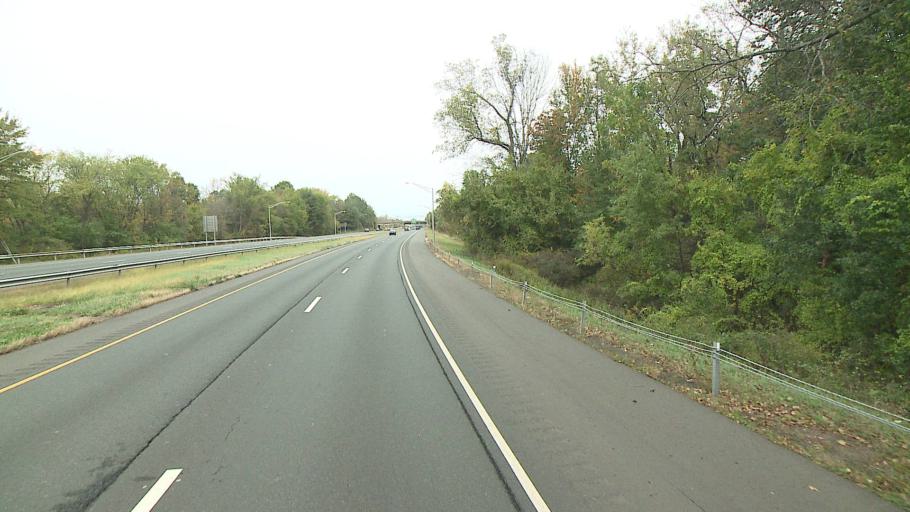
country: US
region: Connecticut
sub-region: Hartford County
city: Kensington
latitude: 41.6303
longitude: -72.7510
